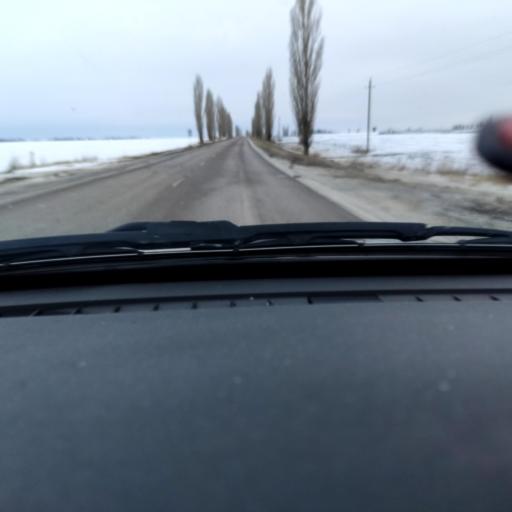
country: RU
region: Voronezj
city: Novaya Usman'
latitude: 51.5519
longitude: 39.3704
